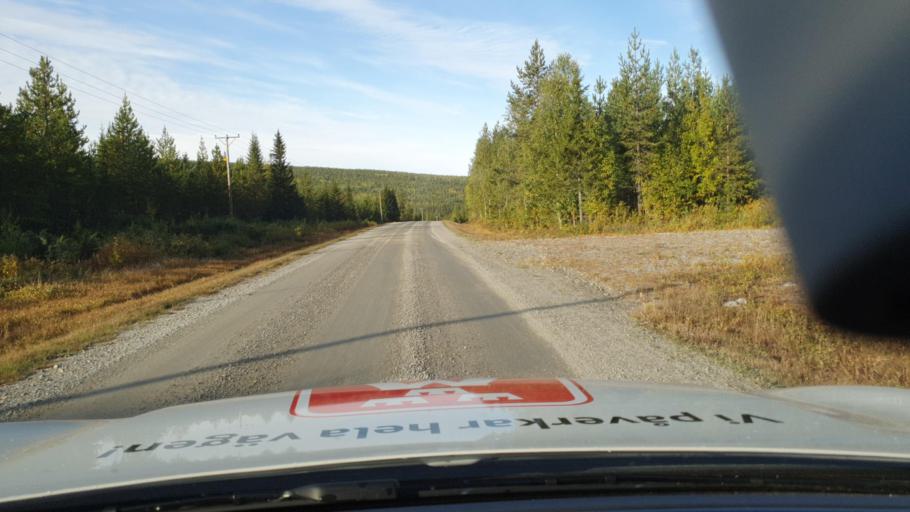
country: SE
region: Vaesterbotten
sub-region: Asele Kommun
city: Insjon
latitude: 64.0847
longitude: 17.8342
